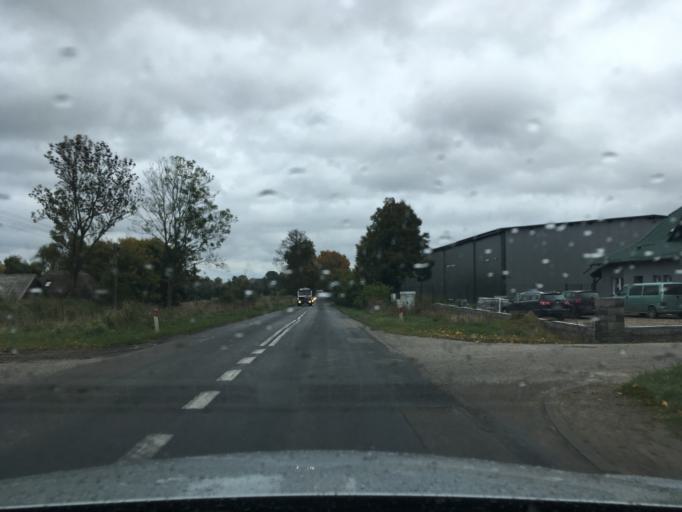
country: PL
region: Pomeranian Voivodeship
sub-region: Powiat koscierski
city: Koscierzyna
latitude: 54.1254
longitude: 18.0538
